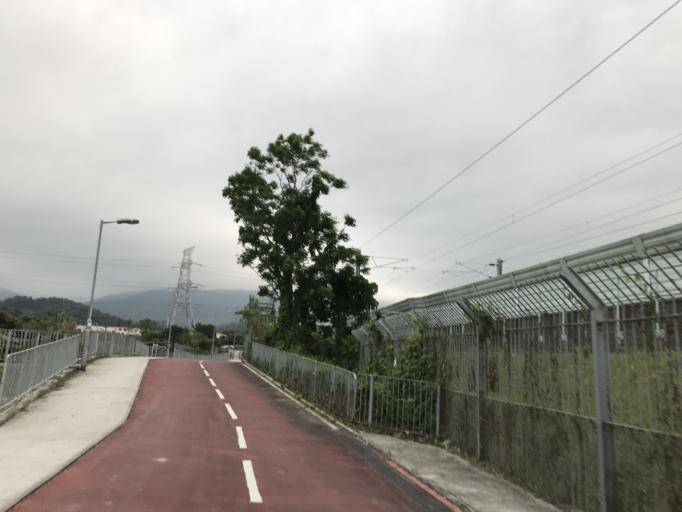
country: HK
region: Tai Po
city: Tai Po
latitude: 22.4699
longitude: 114.1534
